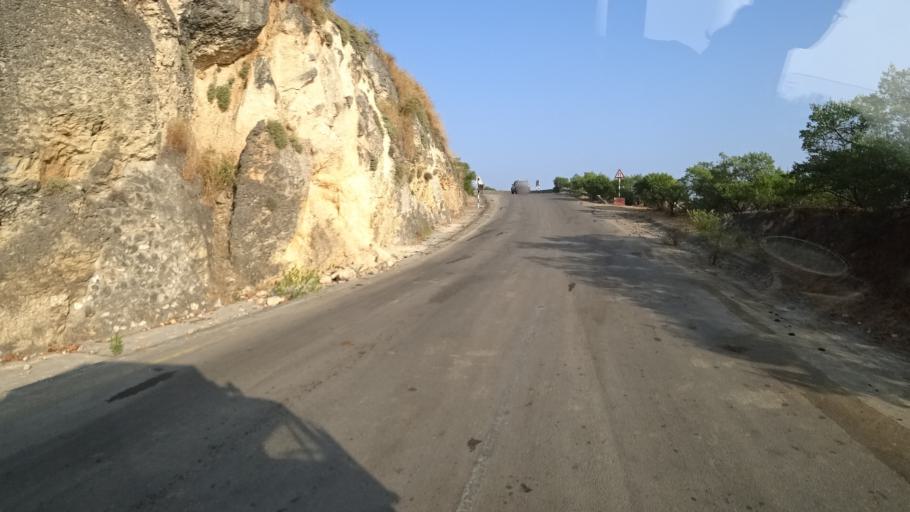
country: YE
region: Al Mahrah
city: Hawf
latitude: 16.7649
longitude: 53.3378
